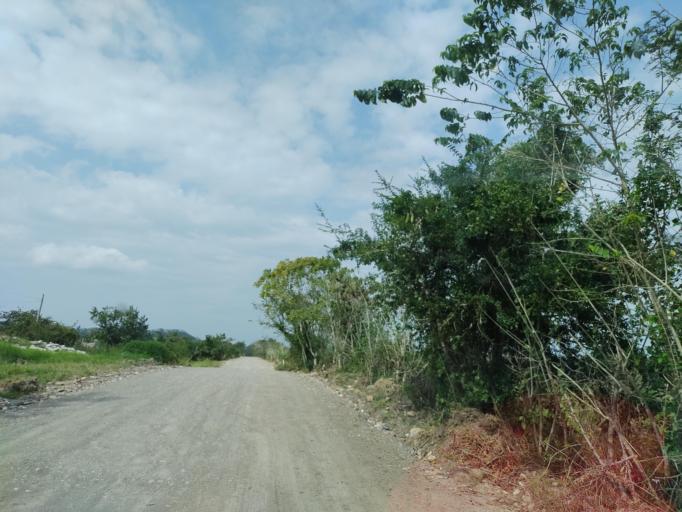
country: MX
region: Puebla
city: Espinal
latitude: 20.2816
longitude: -97.3341
